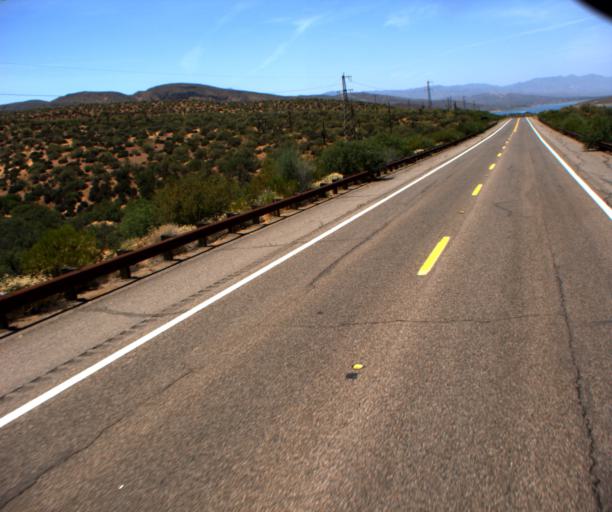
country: US
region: Arizona
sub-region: Gila County
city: Tonto Basin
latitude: 33.6583
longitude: -111.1122
